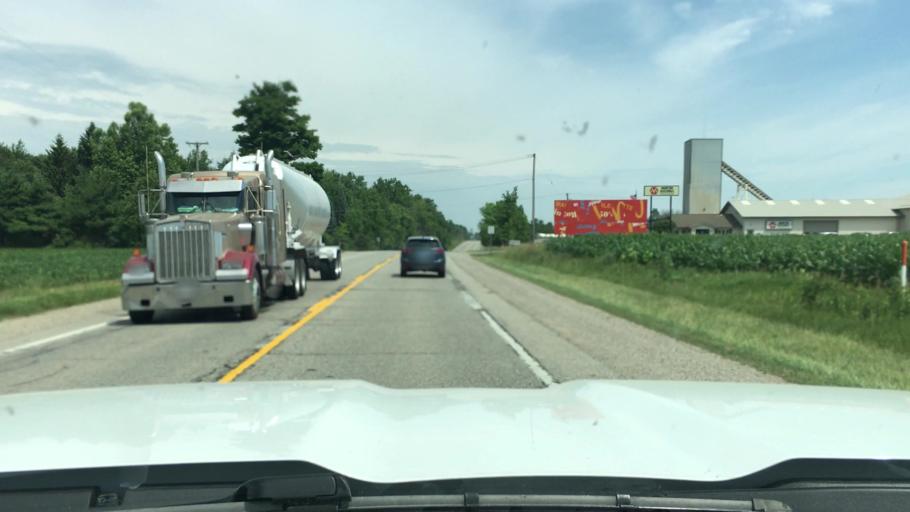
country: US
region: Michigan
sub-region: Sanilac County
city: Marlette
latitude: 43.2471
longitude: -83.0791
